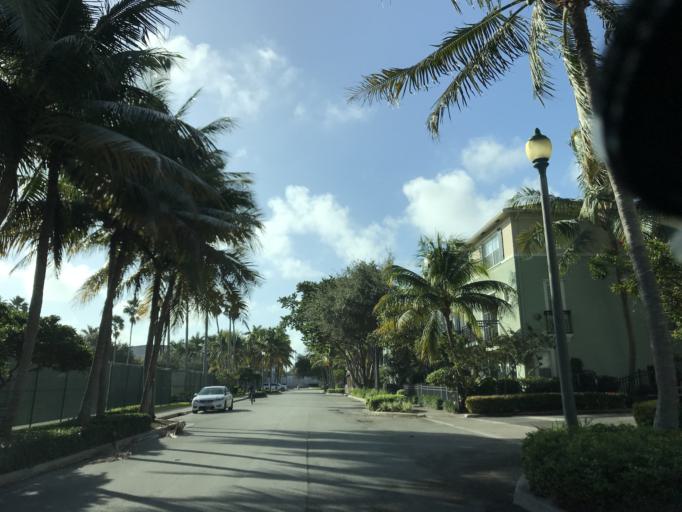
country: US
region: Florida
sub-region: Palm Beach County
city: Delray Beach
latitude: 26.4628
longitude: -80.0762
